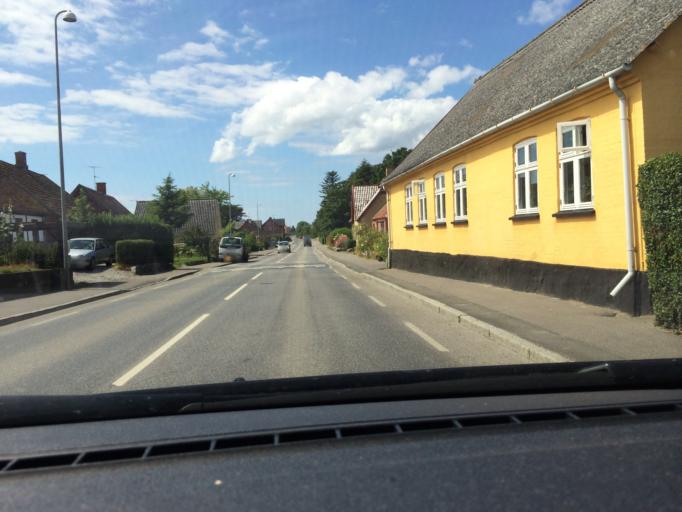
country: DK
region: Zealand
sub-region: Vordingborg Kommune
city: Stege
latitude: 54.9917
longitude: 12.3443
